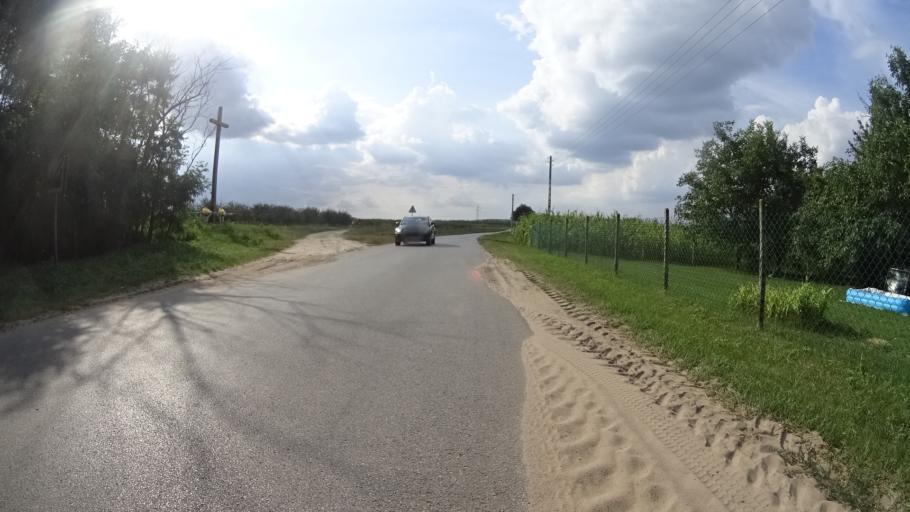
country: PL
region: Masovian Voivodeship
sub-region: Powiat grojecki
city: Mogielnica
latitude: 51.6592
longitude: 20.7503
